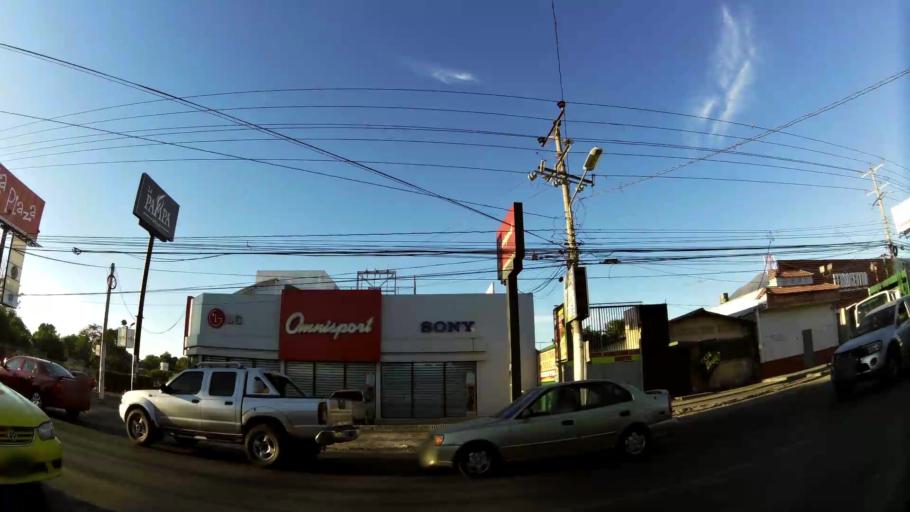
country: SV
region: San Miguel
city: San Miguel
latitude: 13.4660
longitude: -88.1729
